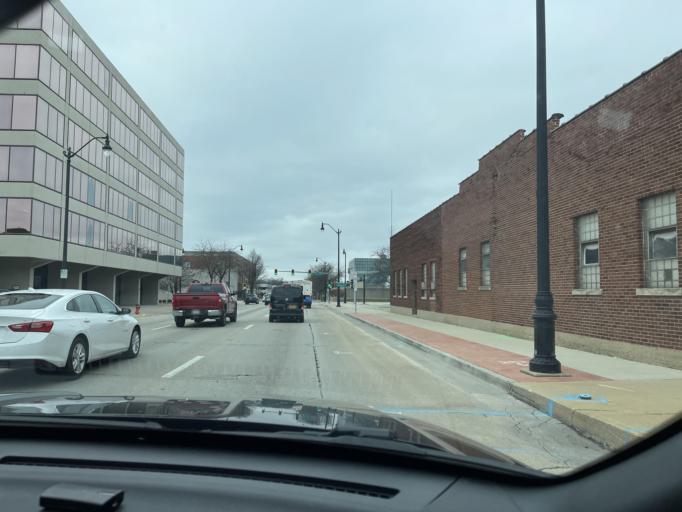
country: US
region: Illinois
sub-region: Sangamon County
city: Springfield
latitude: 39.8029
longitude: -89.6537
